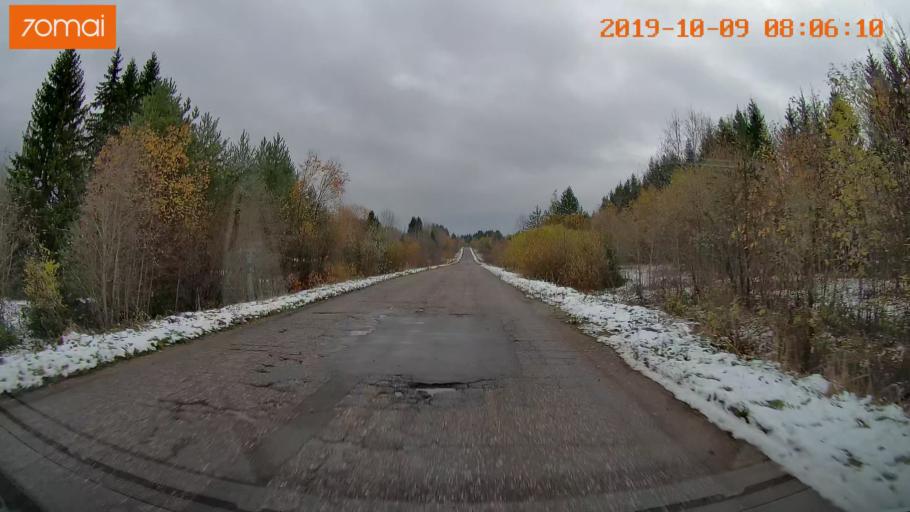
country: RU
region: Jaroslavl
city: Kukoboy
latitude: 58.6928
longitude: 40.0576
